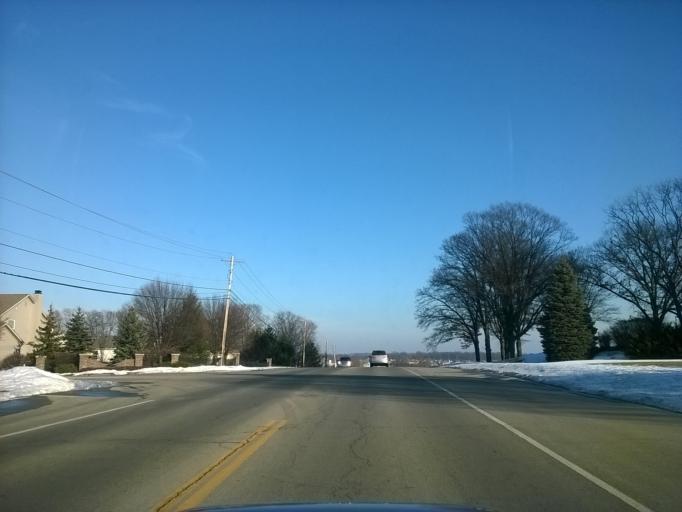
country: US
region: Indiana
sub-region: Hamilton County
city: Carmel
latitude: 39.9785
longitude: -86.0749
